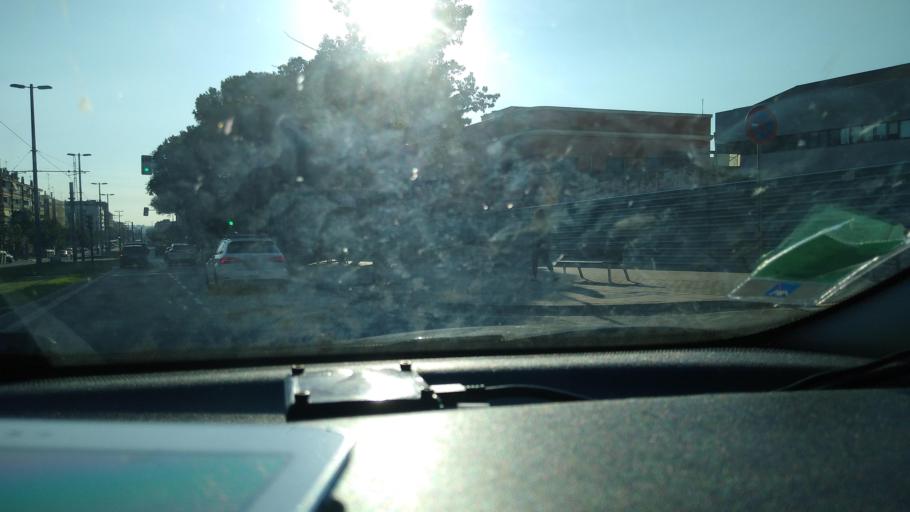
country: ES
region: Catalonia
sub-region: Provincia de Barcelona
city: Esplugues de Llobregat
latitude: 41.3717
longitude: 2.0829
